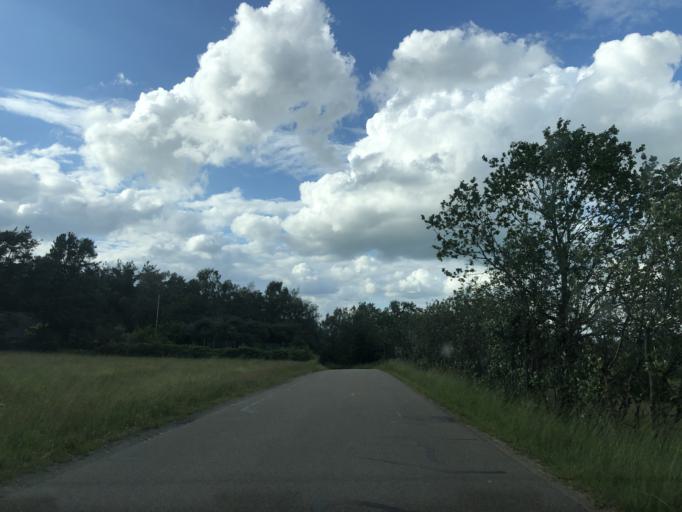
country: DK
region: Central Jutland
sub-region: Silkeborg Kommune
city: Svejbaek
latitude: 56.2131
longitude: 9.6844
